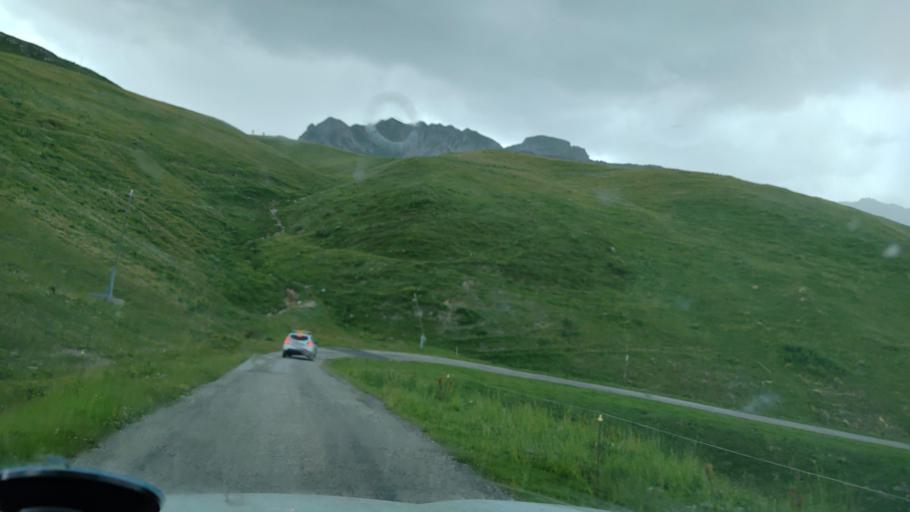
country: FR
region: Rhone-Alpes
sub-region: Departement de la Savoie
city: Courchevel
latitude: 45.3942
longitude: 6.6556
